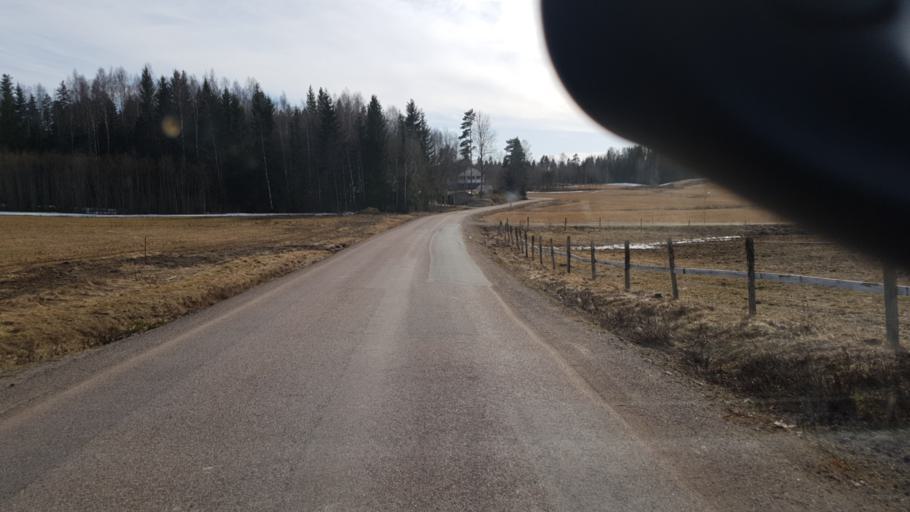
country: SE
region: Vaermland
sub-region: Eda Kommun
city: Charlottenberg
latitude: 59.8690
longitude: 12.3493
